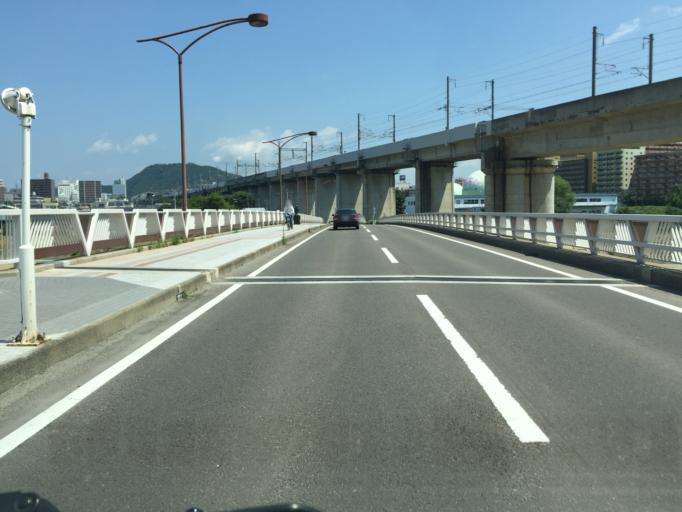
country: JP
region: Fukushima
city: Fukushima-shi
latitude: 37.7455
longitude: 140.4578
